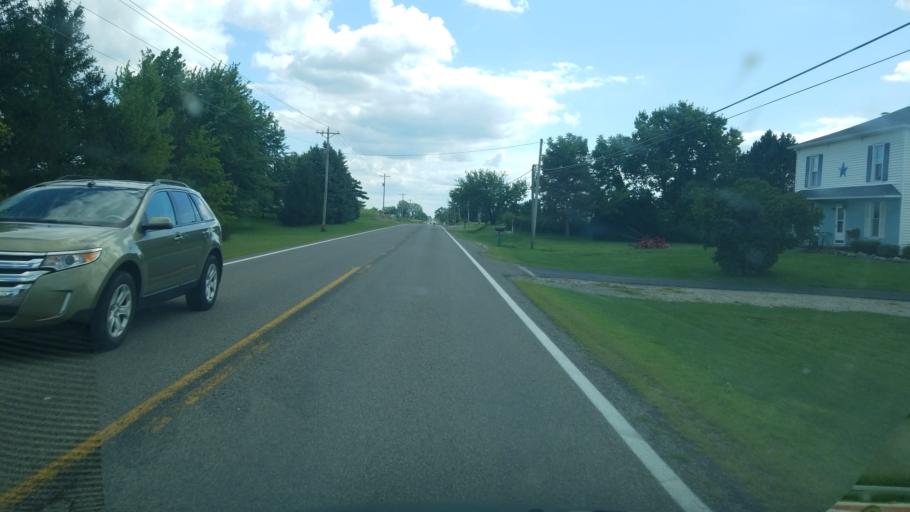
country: US
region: Ohio
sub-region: Allen County
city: Lima
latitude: 40.6412
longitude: -83.9755
